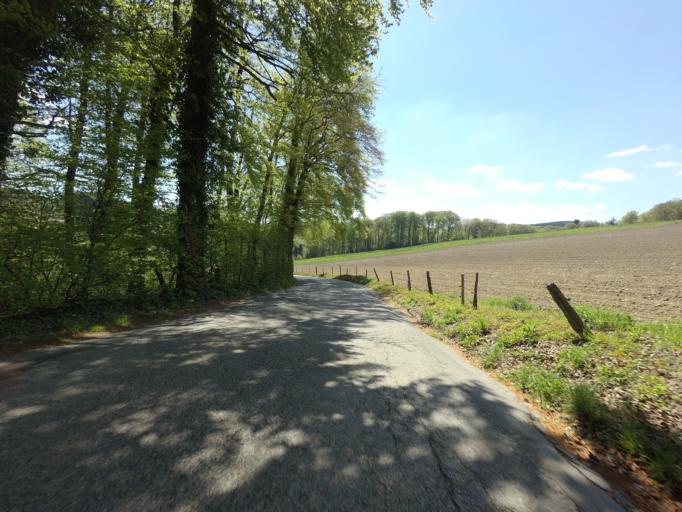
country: DE
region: North Rhine-Westphalia
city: Hemer
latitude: 51.3374
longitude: 7.7715
